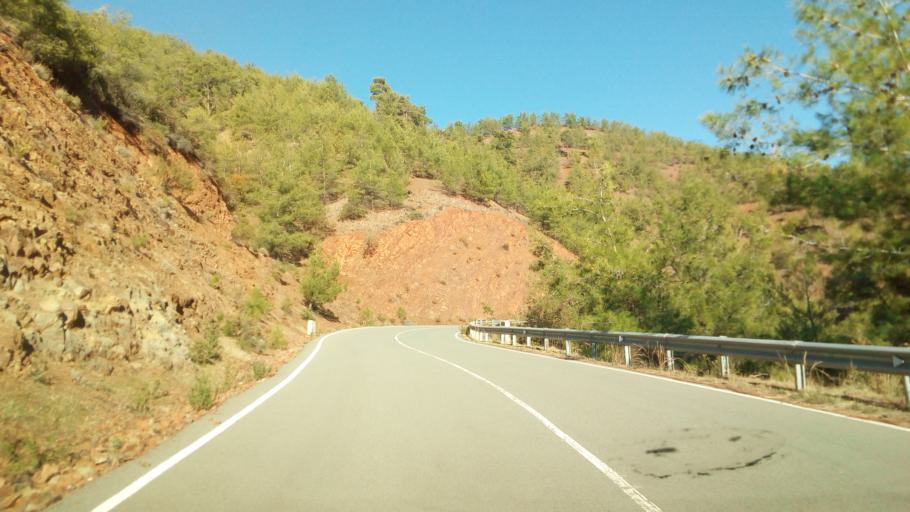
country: CY
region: Lefkosia
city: Lefka
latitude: 35.0976
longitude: 32.7574
